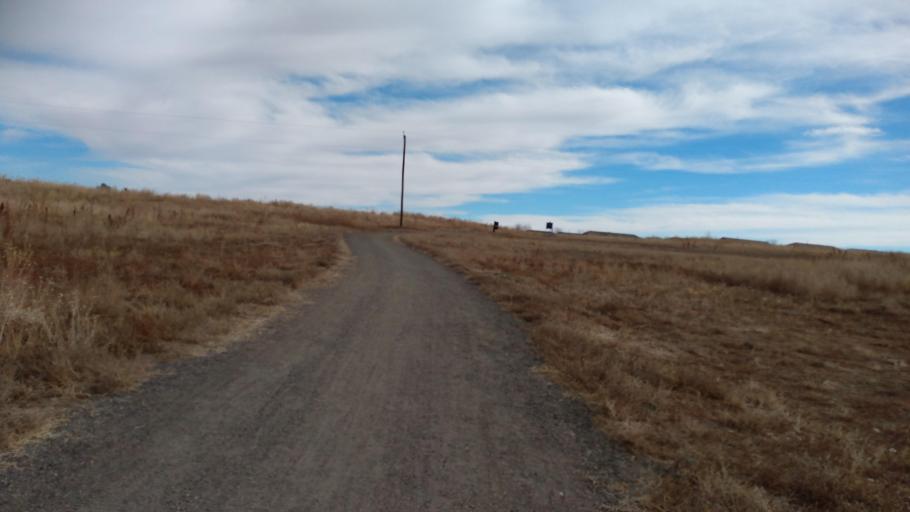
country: US
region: Colorado
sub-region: Boulder County
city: Lafayette
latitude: 39.9946
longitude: -105.0539
